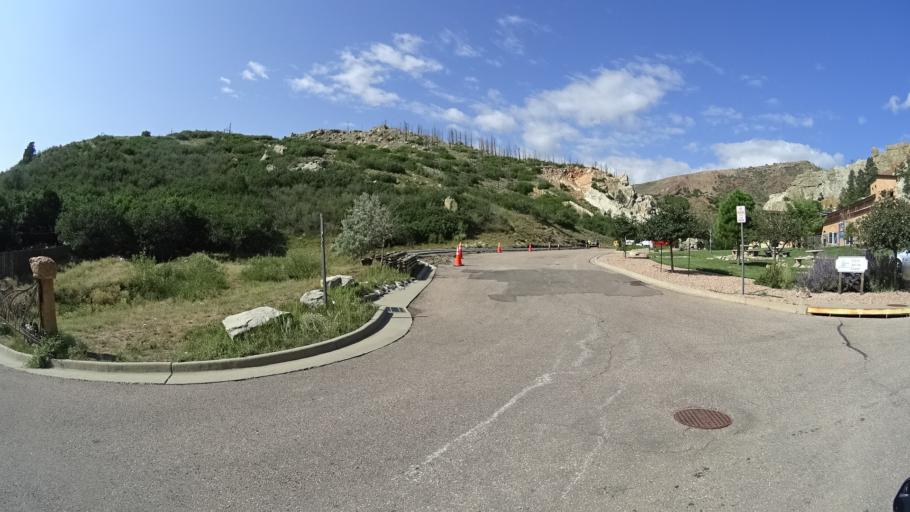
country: US
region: Colorado
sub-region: El Paso County
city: Manitou Springs
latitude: 38.9054
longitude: -104.8773
